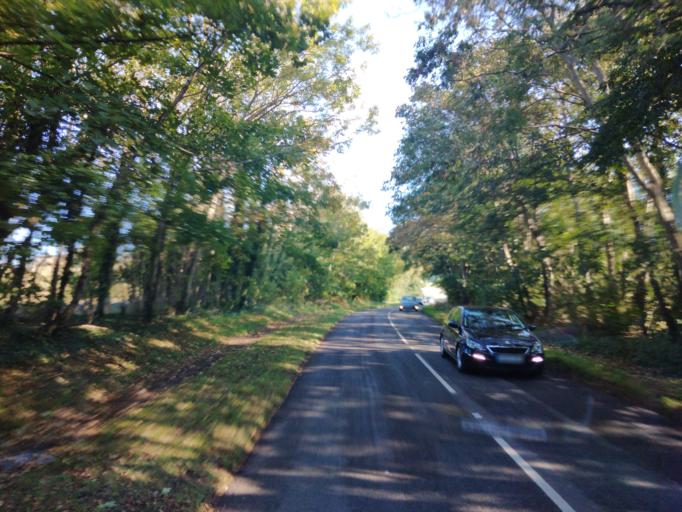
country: GB
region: England
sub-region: East Sussex
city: Seaford
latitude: 50.7835
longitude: 0.1274
